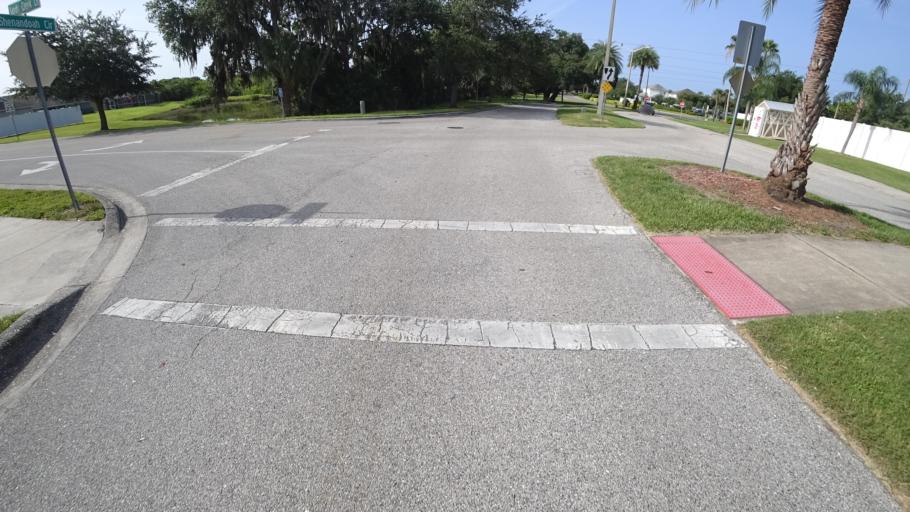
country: US
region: Florida
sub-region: Manatee County
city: Ellenton
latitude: 27.5533
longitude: -82.4994
